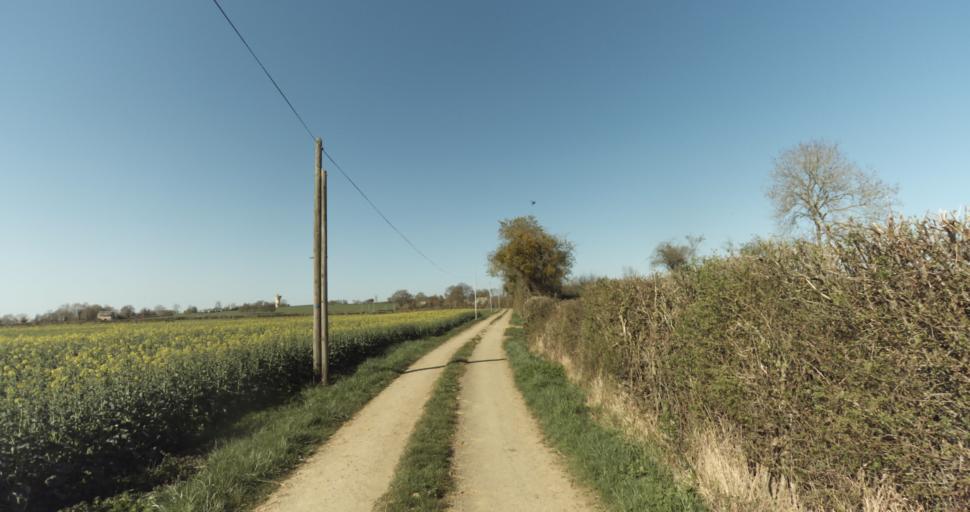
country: FR
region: Lower Normandy
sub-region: Departement du Calvados
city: Saint-Pierre-sur-Dives
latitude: 48.9325
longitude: -0.0059
